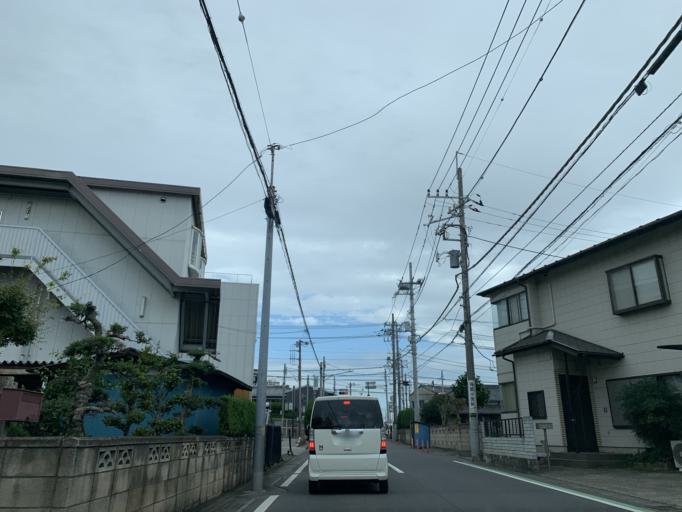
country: JP
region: Chiba
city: Kashiwa
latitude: 35.8821
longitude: 139.9514
